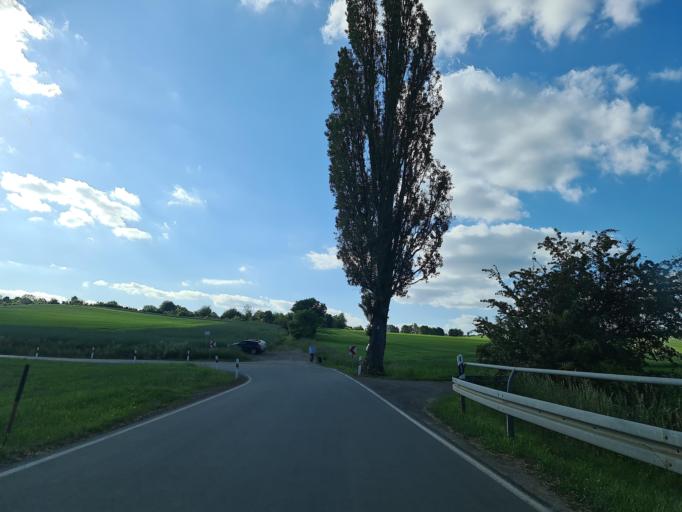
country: DE
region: Saxony
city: Weischlitz
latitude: 50.4902
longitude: 12.0722
